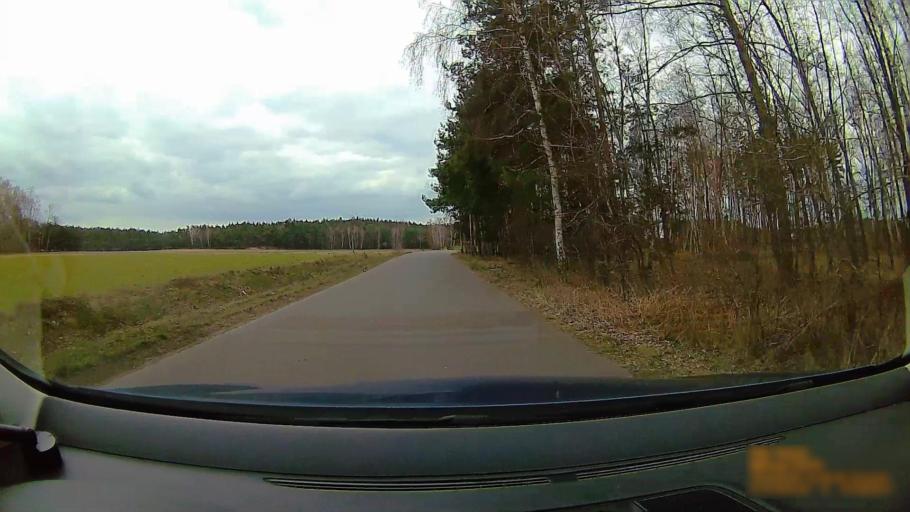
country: PL
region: Greater Poland Voivodeship
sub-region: Powiat koninski
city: Rychwal
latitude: 52.0859
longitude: 18.1407
